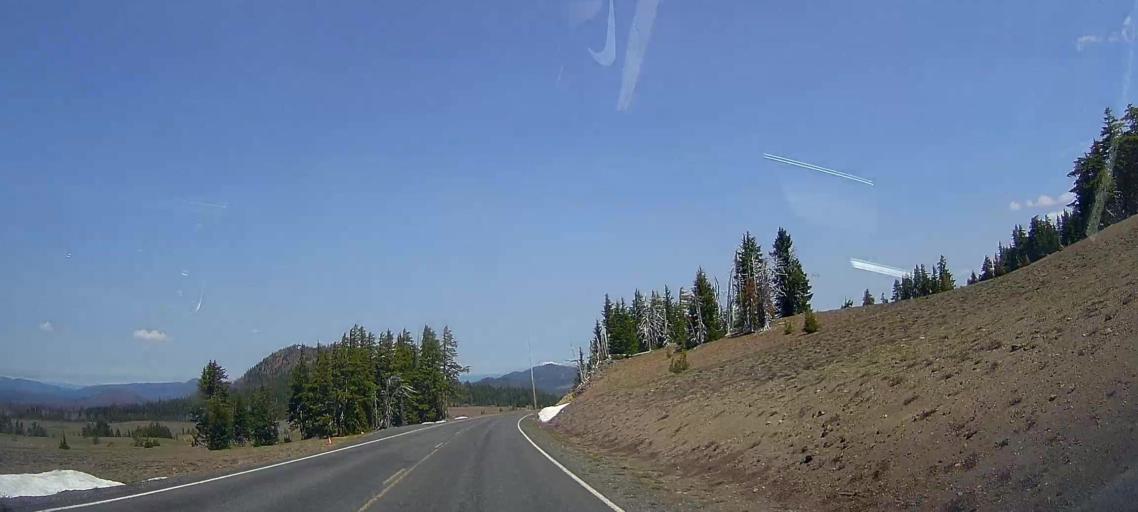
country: US
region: Oregon
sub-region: Jackson County
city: Shady Cove
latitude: 42.9768
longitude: -122.1531
